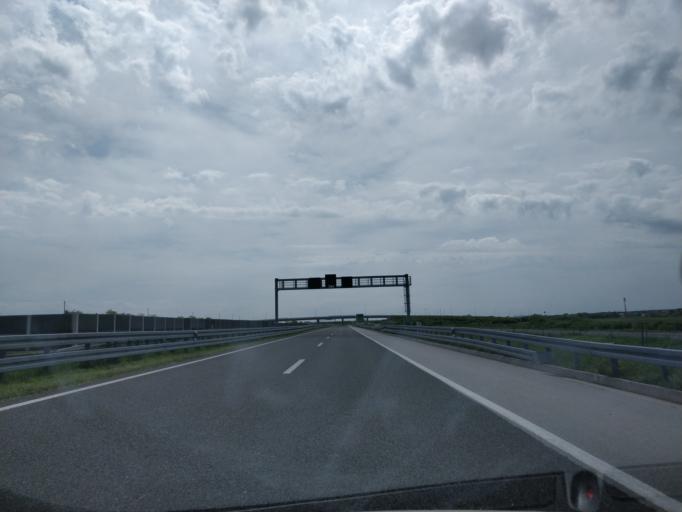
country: HR
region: Zagrebacka
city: Gradici
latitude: 45.7024
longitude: 16.0542
